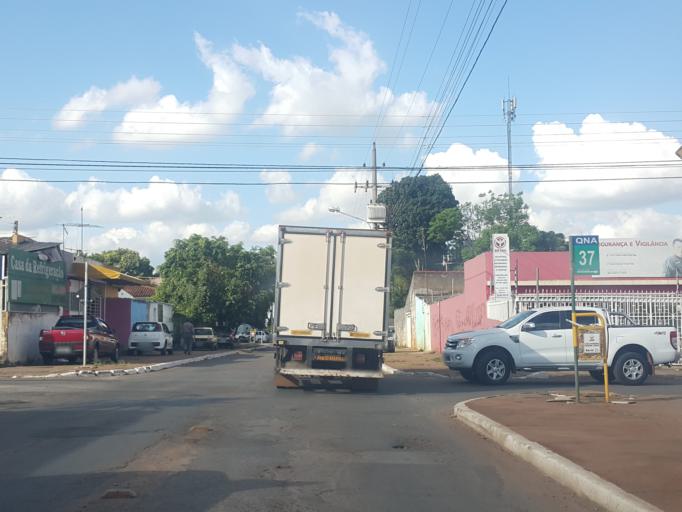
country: BR
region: Federal District
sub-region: Brasilia
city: Brasilia
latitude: -15.8223
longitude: -48.0581
